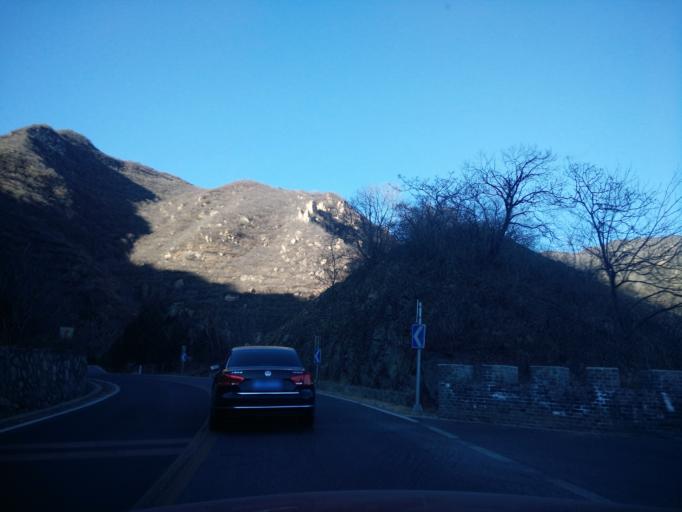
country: CN
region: Beijing
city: Wangping
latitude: 40.0056
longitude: 115.9721
